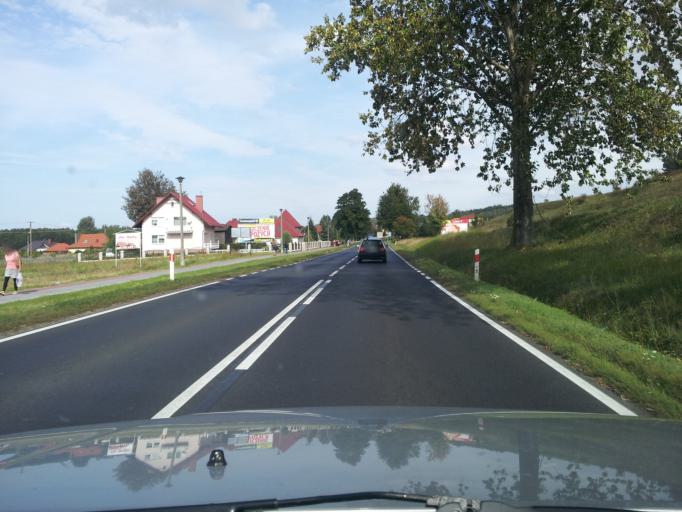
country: PL
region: Warmian-Masurian Voivodeship
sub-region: Powiat nowomiejski
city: Kurzetnik
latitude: 53.4021
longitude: 19.5860
